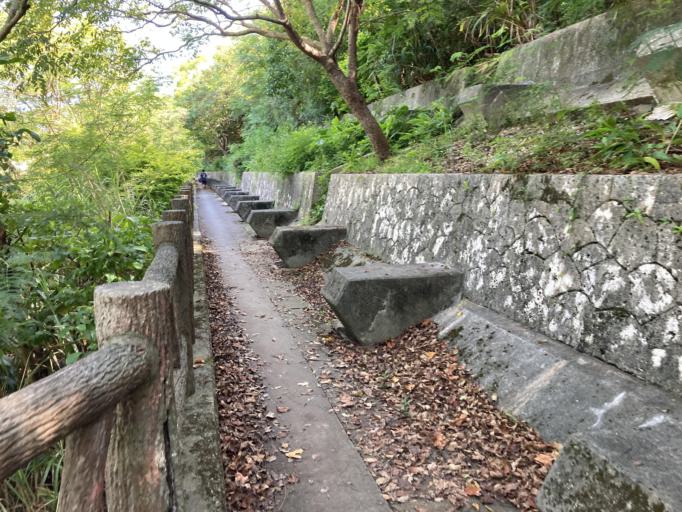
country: JP
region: Okinawa
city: Naha-shi
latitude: 26.2116
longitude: 127.7174
